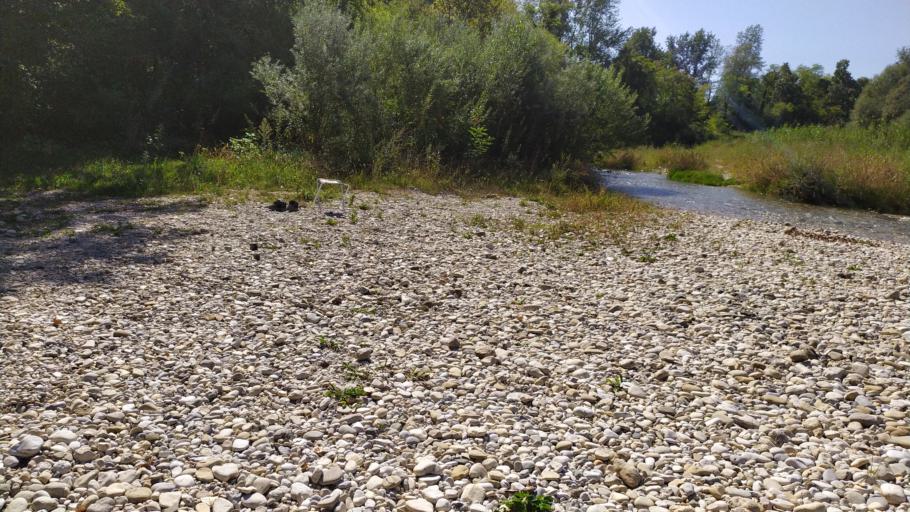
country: IT
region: Friuli Venezia Giulia
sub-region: Provincia di Pordenone
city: Cavolano-Schiavoi
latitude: 45.9388
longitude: 12.4875
